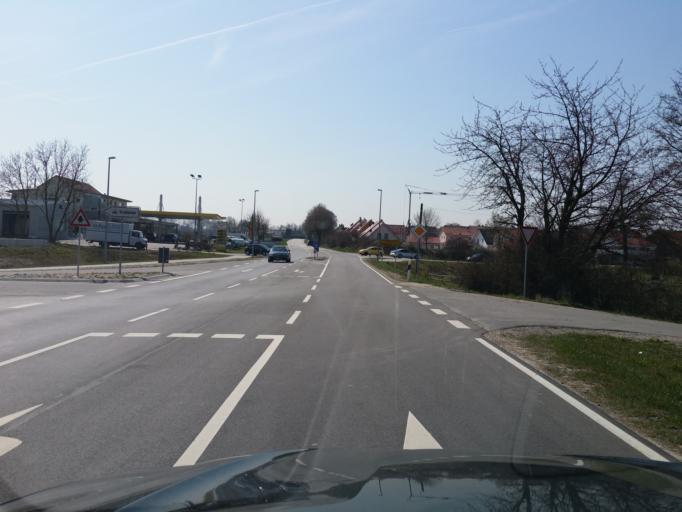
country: DE
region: Bavaria
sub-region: Upper Bavaria
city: Langenpreising
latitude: 48.4320
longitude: 11.9784
